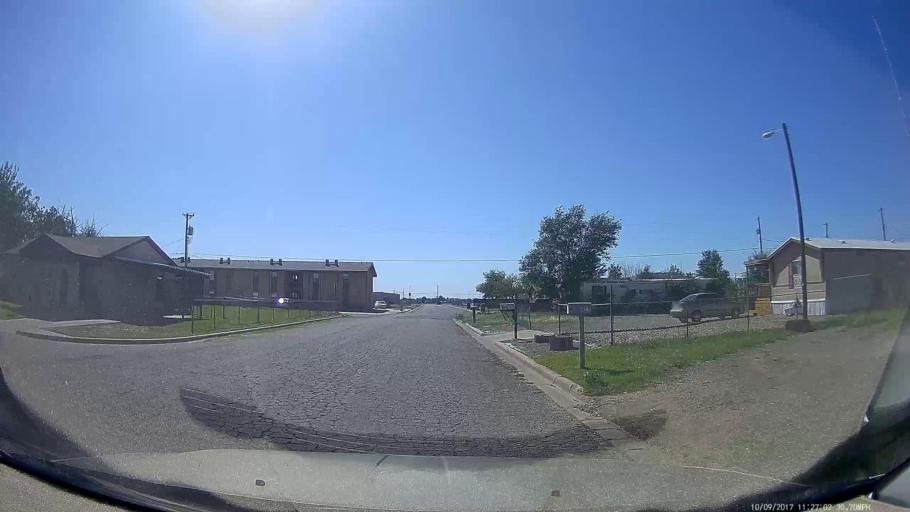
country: US
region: New Mexico
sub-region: Curry County
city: Clovis
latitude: 34.4065
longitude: -103.2273
